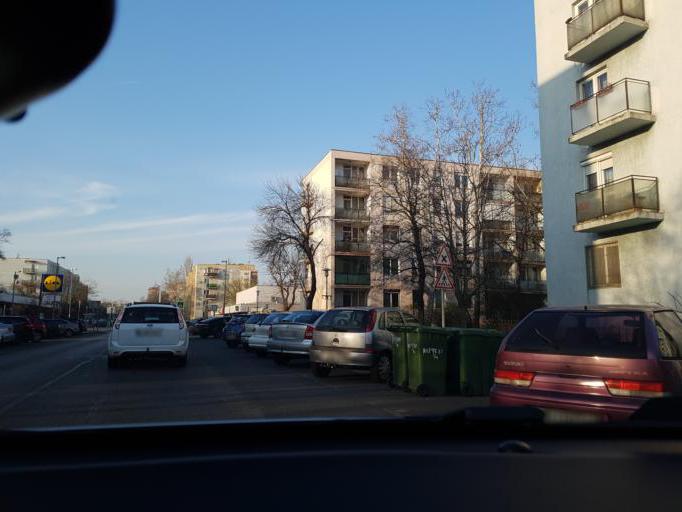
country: HU
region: Budapest
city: Budapest XX. keruelet
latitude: 47.4615
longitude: 19.1151
